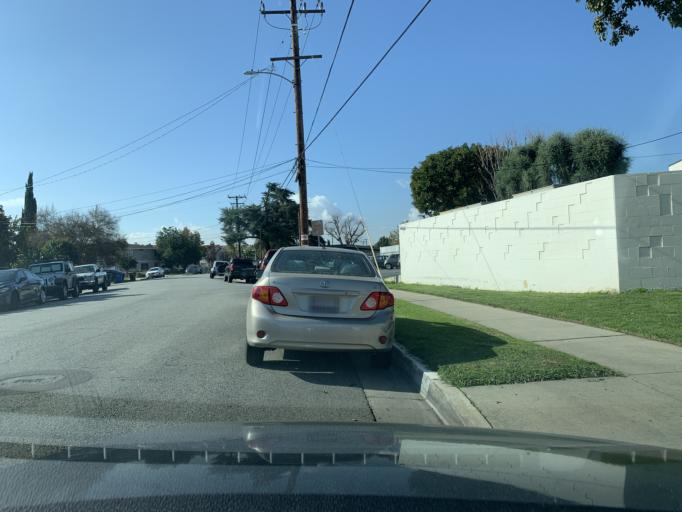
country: US
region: California
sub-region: Los Angeles County
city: South El Monte
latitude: 34.0651
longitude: -118.0561
